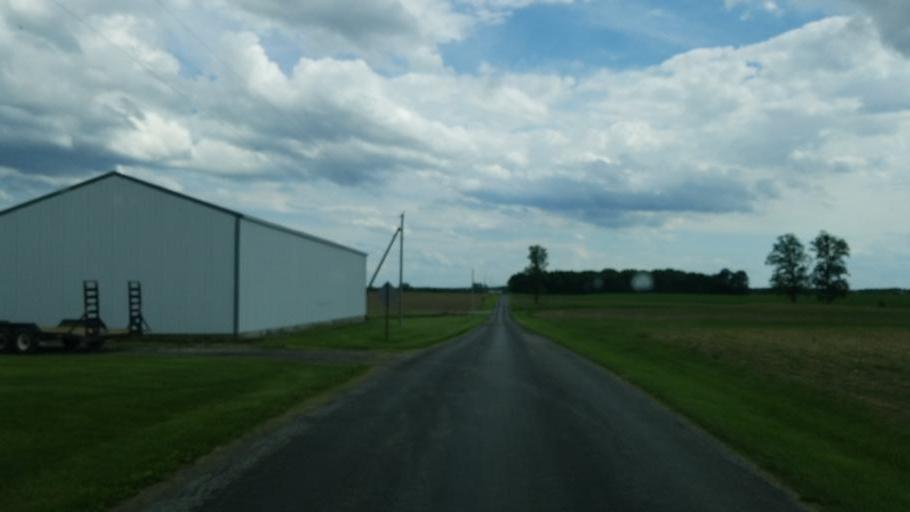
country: US
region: Ohio
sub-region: Richland County
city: Shelby
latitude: 40.9376
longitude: -82.5714
